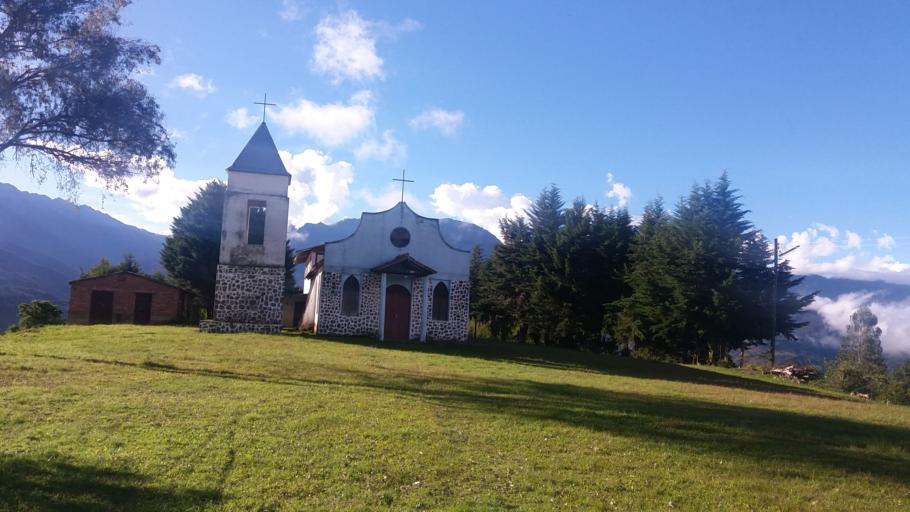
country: BO
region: Cochabamba
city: Colomi
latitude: -17.0854
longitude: -65.9990
